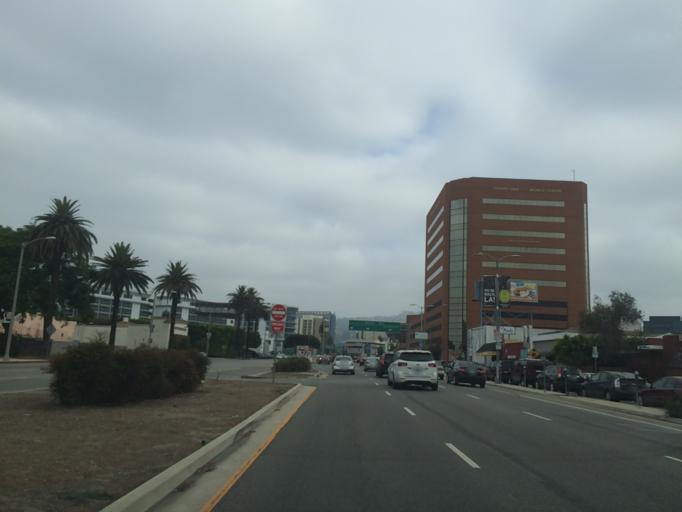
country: US
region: California
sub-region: Los Angeles County
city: West Hollywood
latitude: 34.0684
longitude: -118.3747
